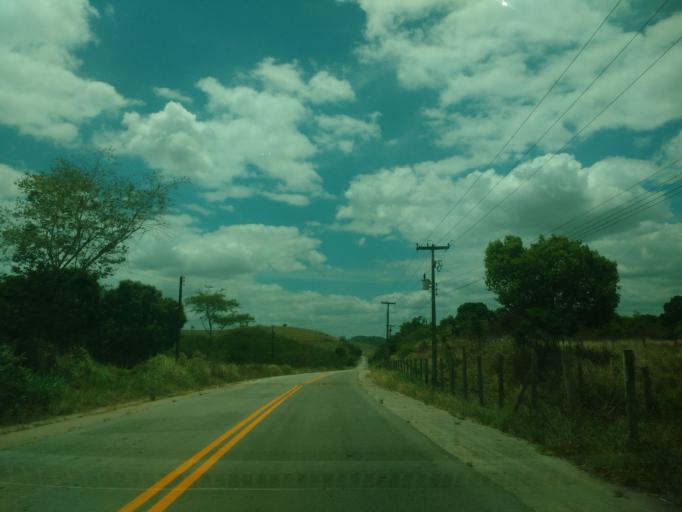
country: BR
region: Alagoas
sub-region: Uniao Dos Palmares
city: Uniao dos Palmares
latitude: -9.1423
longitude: -36.0495
